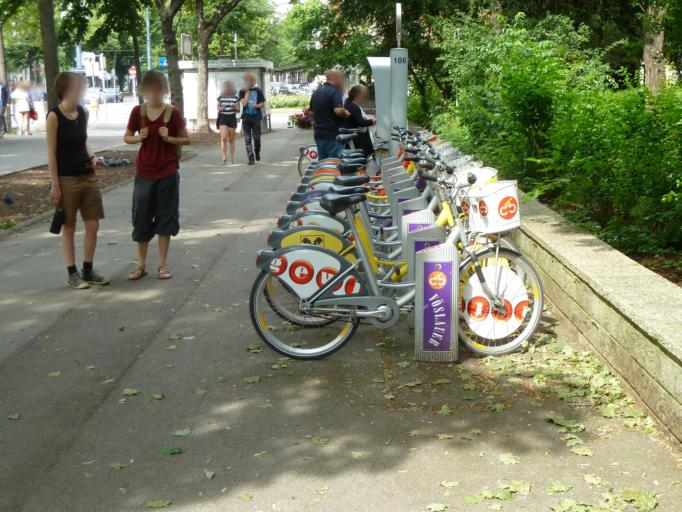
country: AT
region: Vienna
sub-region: Wien Stadt
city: Vienna
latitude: 48.2067
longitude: 16.3803
